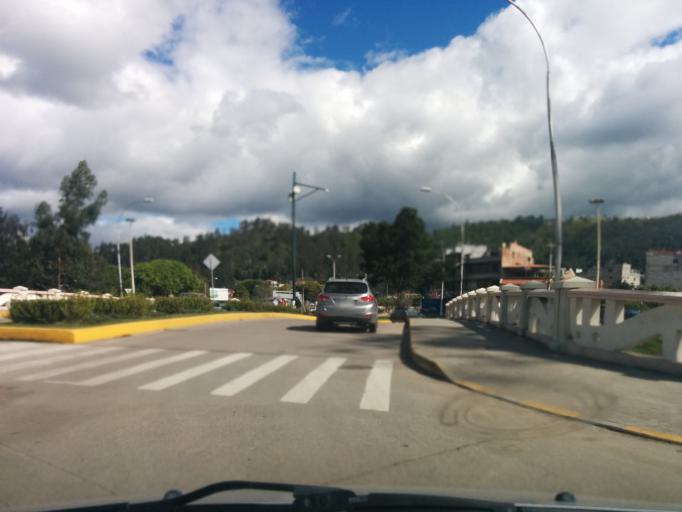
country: EC
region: Azuay
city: Cuenca
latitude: -2.9097
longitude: -78.9942
